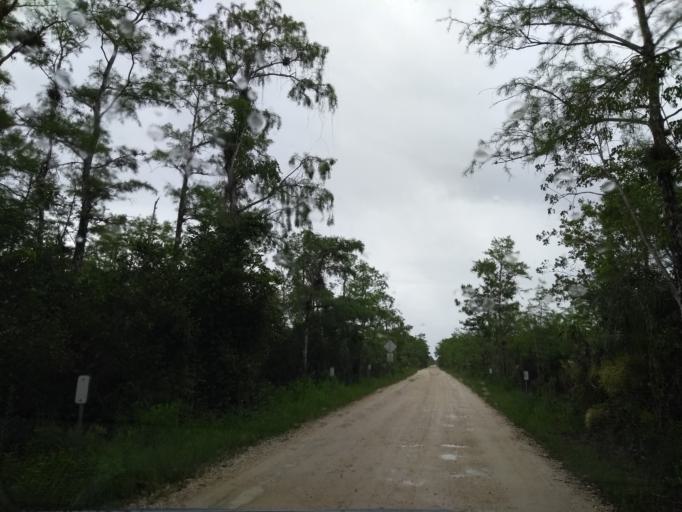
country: US
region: Florida
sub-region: Miami-Dade County
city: The Hammocks
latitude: 25.7604
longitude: -81.0091
